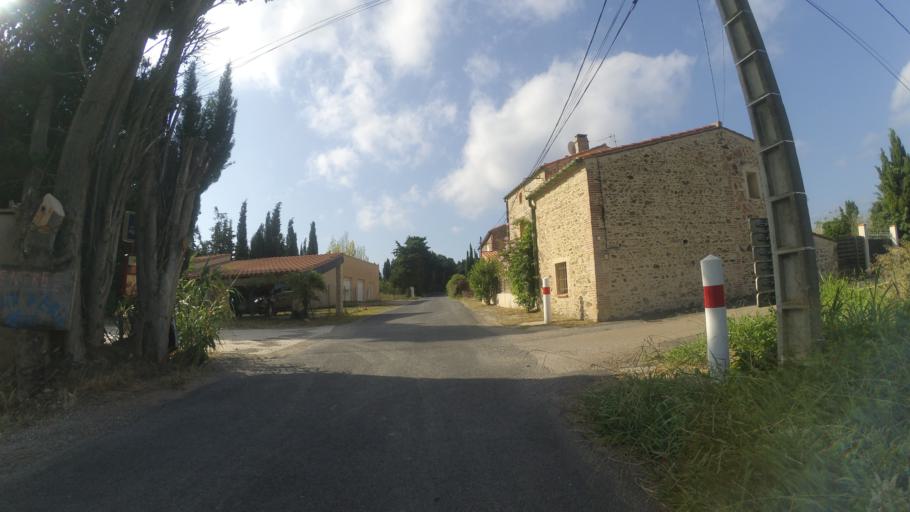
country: FR
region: Languedoc-Roussillon
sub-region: Departement des Pyrenees-Orientales
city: Millas
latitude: 42.6573
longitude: 2.7083
